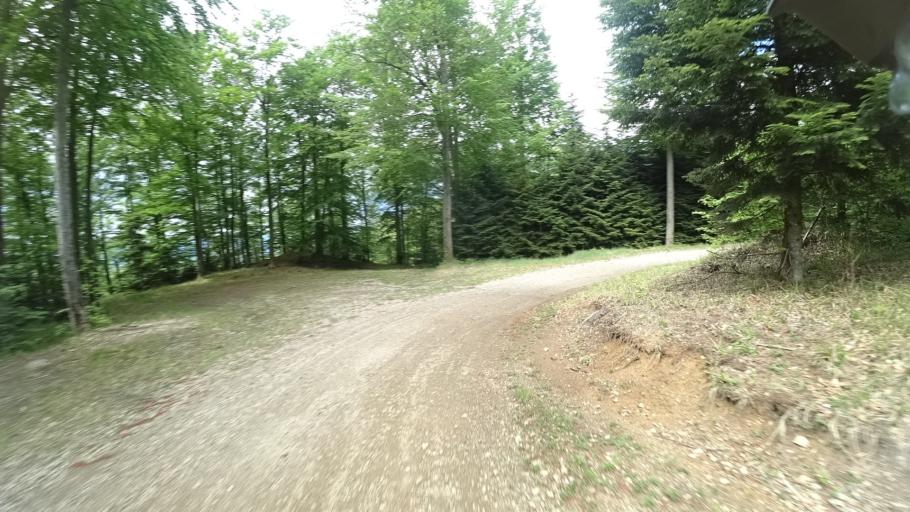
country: HR
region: Grad Zagreb
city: Kasina
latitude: 45.9170
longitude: 15.9388
